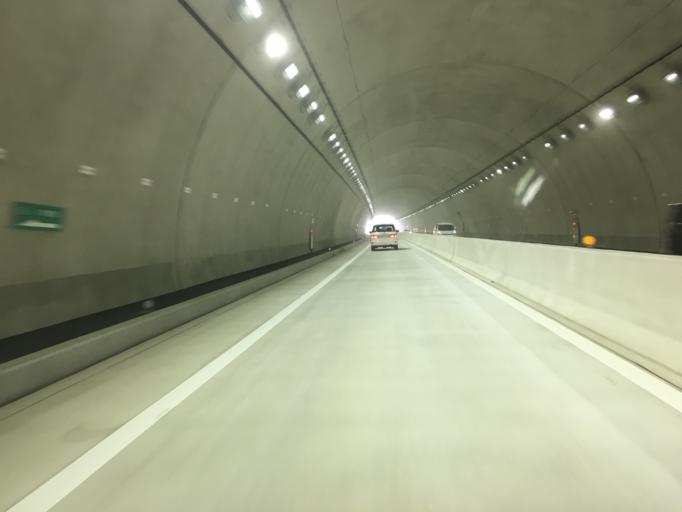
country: JP
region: Fukushima
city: Hobaramachi
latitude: 37.7827
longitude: 140.5704
